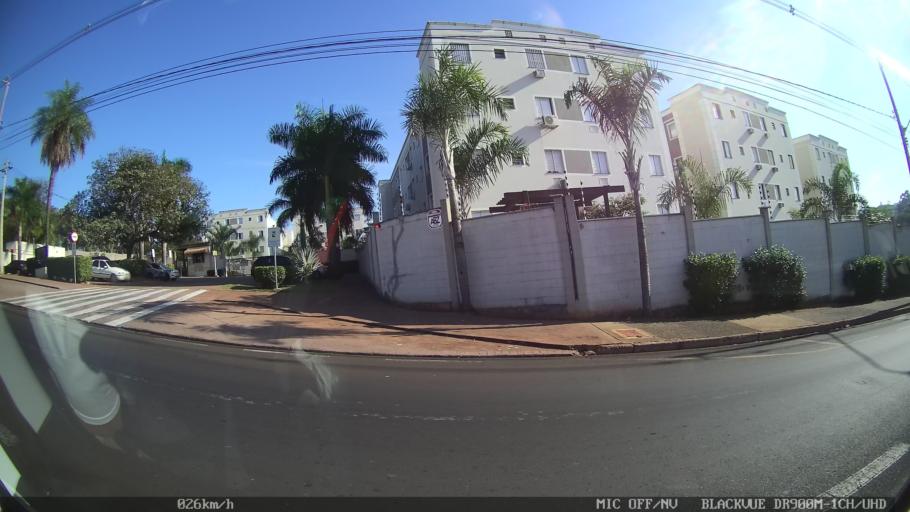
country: BR
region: Sao Paulo
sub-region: Sao Jose Do Rio Preto
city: Sao Jose do Rio Preto
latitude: -20.7757
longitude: -49.3985
